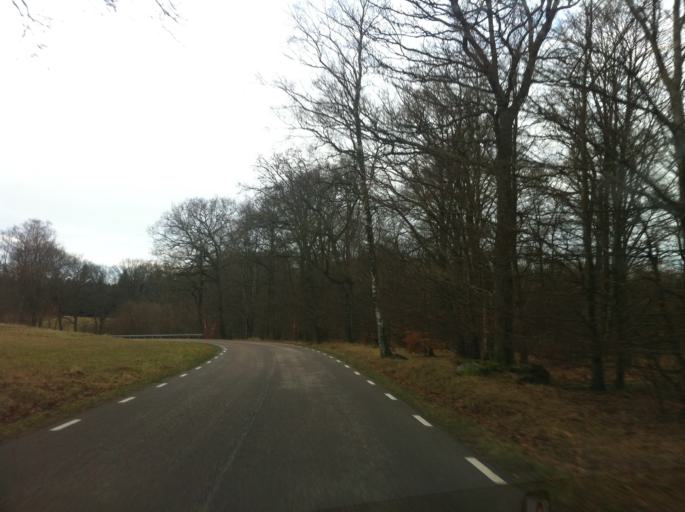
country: SE
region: Skane
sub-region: Svalovs Kommun
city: Kagerod
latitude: 56.0594
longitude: 13.1121
